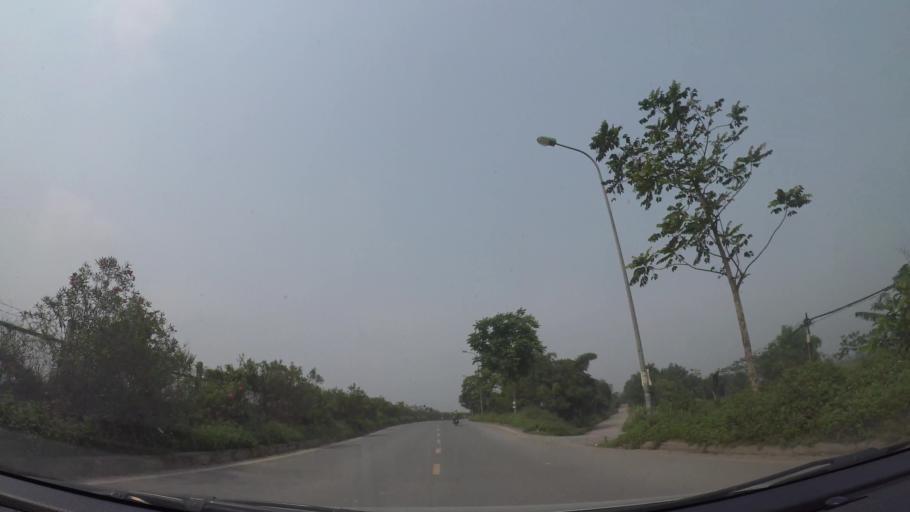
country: VN
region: Ha Noi
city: Quoc Oai
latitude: 20.9980
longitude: 105.5934
